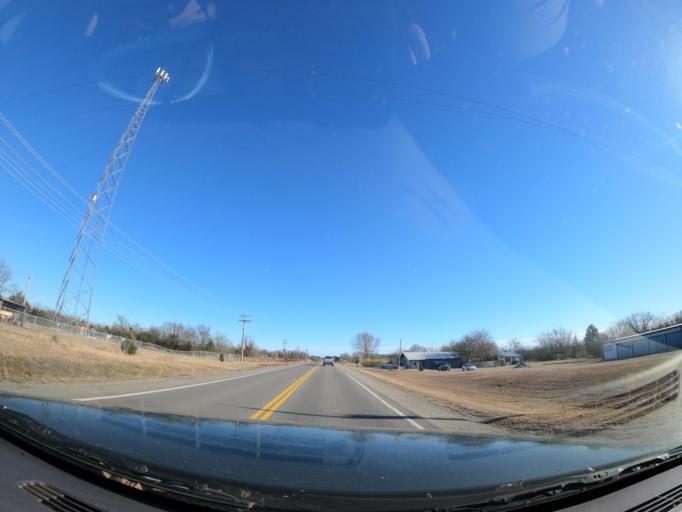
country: US
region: Oklahoma
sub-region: Pittsburg County
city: Longtown
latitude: 35.2360
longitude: -95.4650
